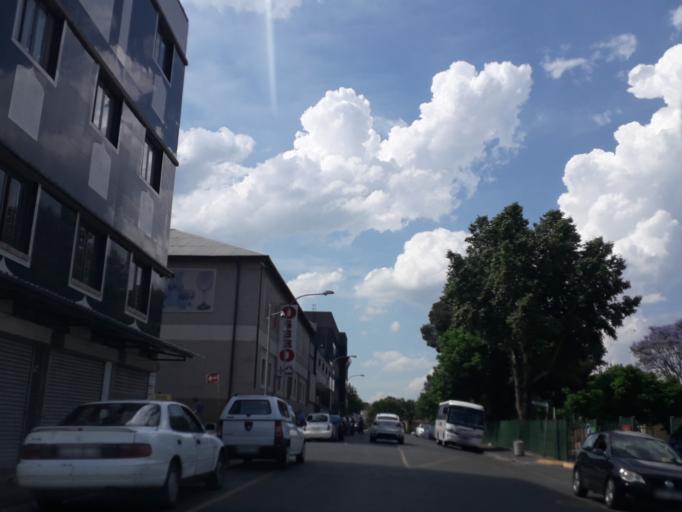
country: ZA
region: Gauteng
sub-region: City of Johannesburg Metropolitan Municipality
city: Johannesburg
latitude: -26.2055
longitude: 28.0235
